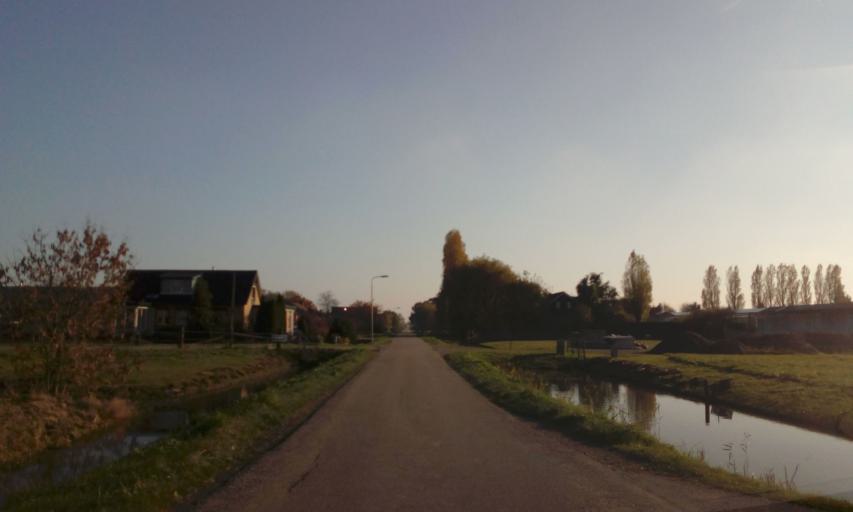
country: NL
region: South Holland
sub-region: Gemeente Waddinxveen
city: Waddinxveen
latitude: 52.0033
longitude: 4.6102
